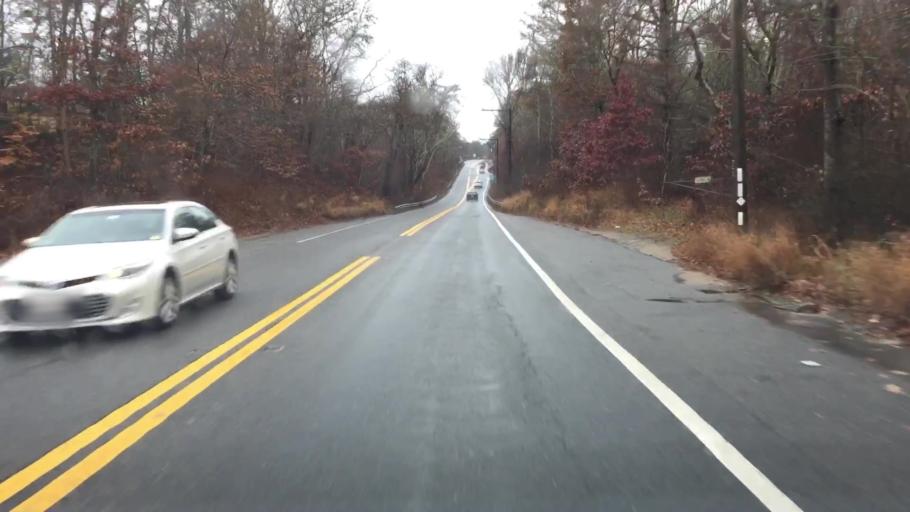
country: US
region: Massachusetts
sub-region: Barnstable County
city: Falmouth
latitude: 41.5755
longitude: -70.6236
